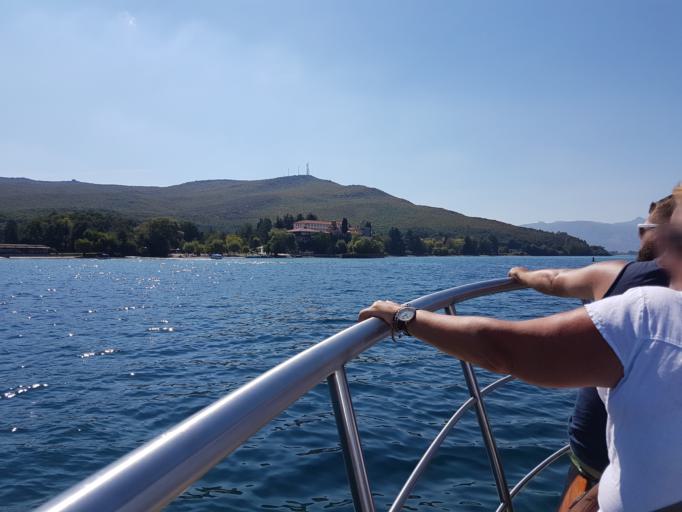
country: AL
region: Korce
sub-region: Rrethi i Pogradecit
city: Bucimas
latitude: 40.9172
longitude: 20.7431
